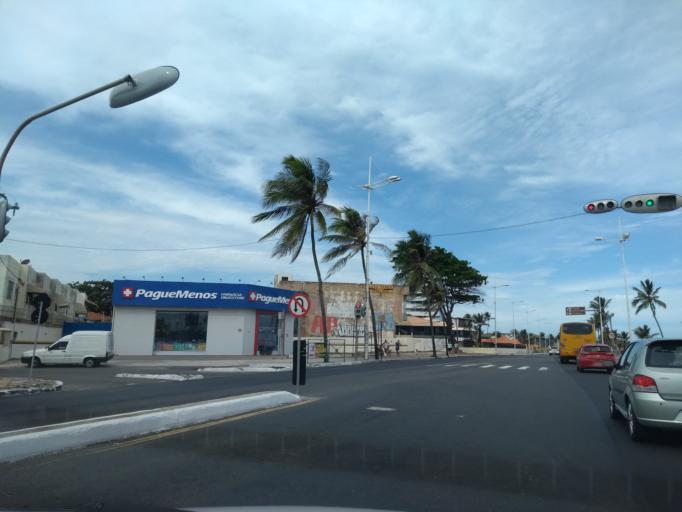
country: BR
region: Bahia
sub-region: Lauro De Freitas
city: Lauro de Freitas
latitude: -12.9528
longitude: -38.3778
